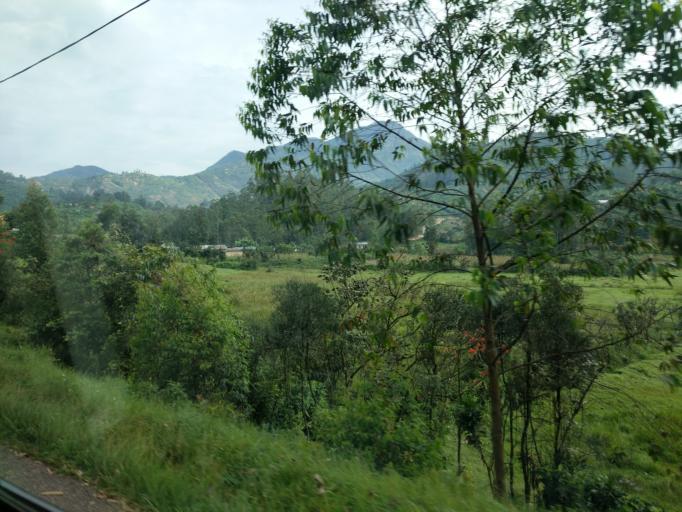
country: RW
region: Northern Province
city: Musanze
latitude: -1.6498
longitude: 29.8049
